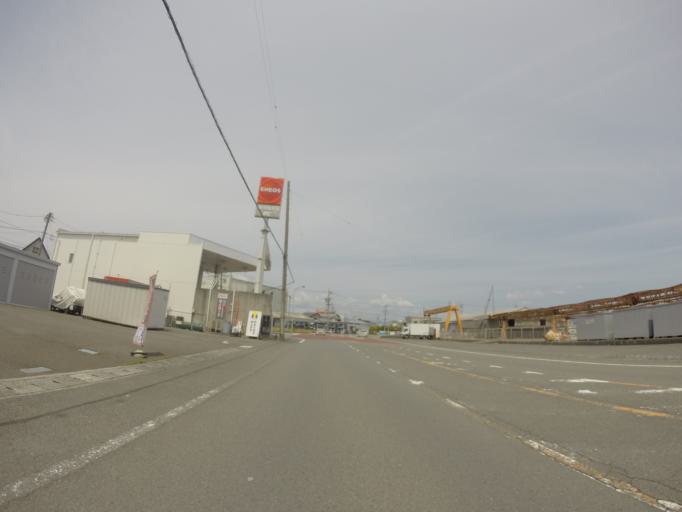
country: JP
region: Shizuoka
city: Yaizu
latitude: 34.8452
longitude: 138.3250
